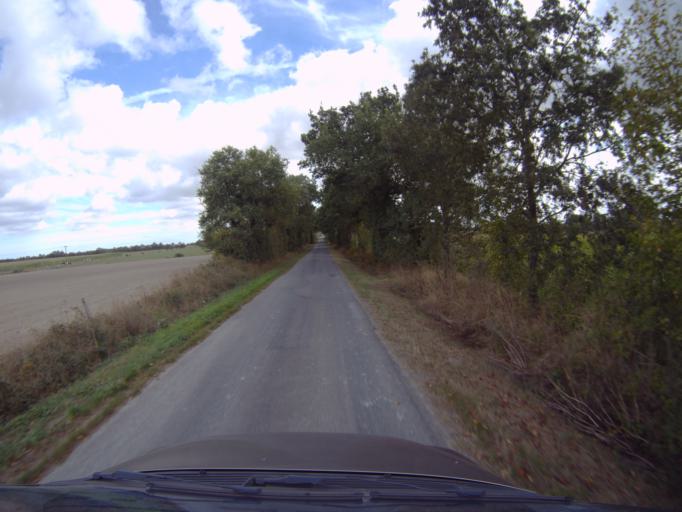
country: FR
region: Pays de la Loire
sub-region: Departement de la Loire-Atlantique
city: La Planche
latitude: 47.0291
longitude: -1.4140
